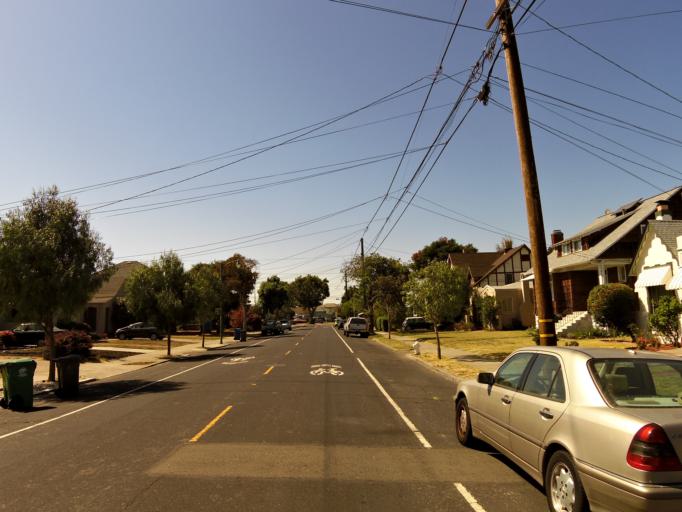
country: US
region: California
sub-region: Alameda County
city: Oakland
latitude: 37.7736
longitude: -122.2868
